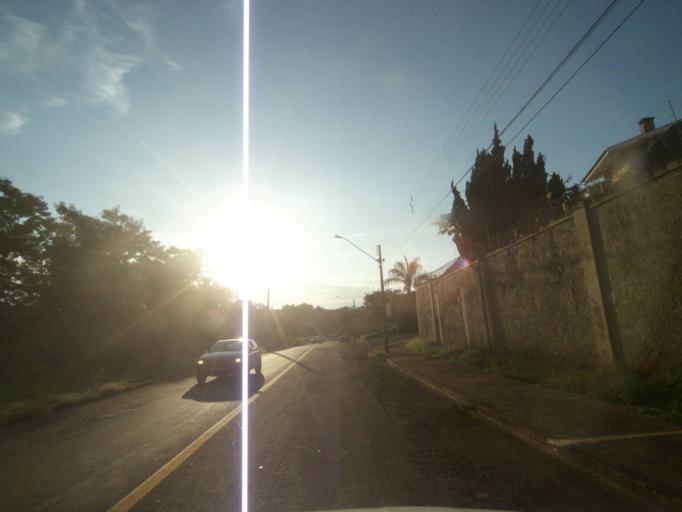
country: BR
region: Parana
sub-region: Londrina
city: Londrina
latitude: -23.3495
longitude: -51.1922
